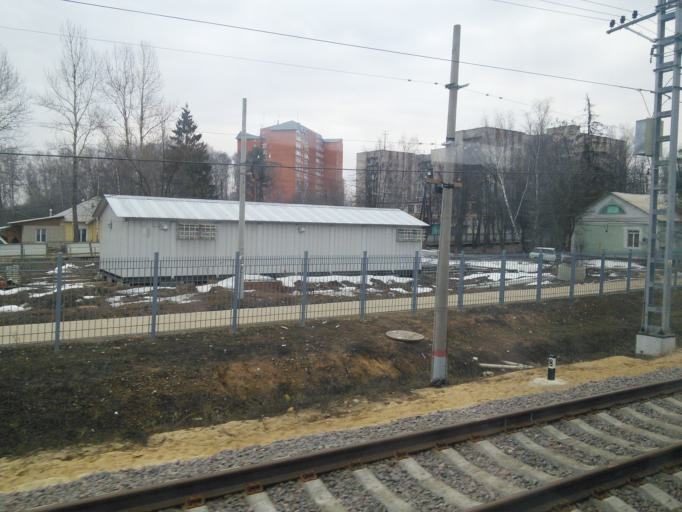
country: RU
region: Moskovskaya
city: Vostryakovo
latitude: 55.4208
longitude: 37.8335
